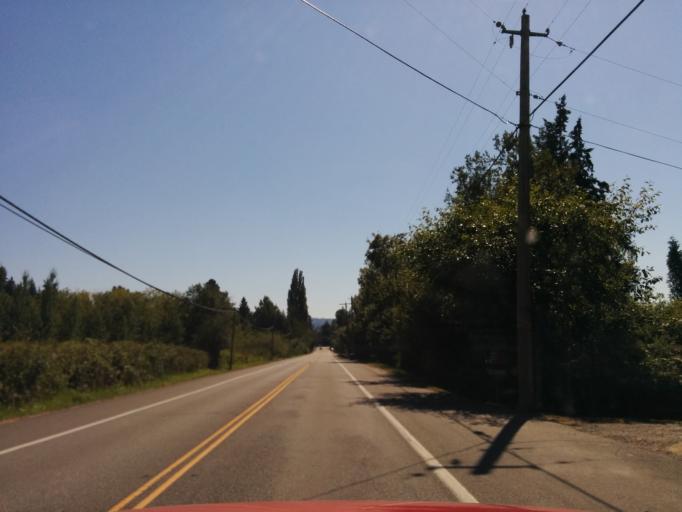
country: US
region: Washington
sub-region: King County
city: Sammamish
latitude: 47.6082
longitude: -122.0726
